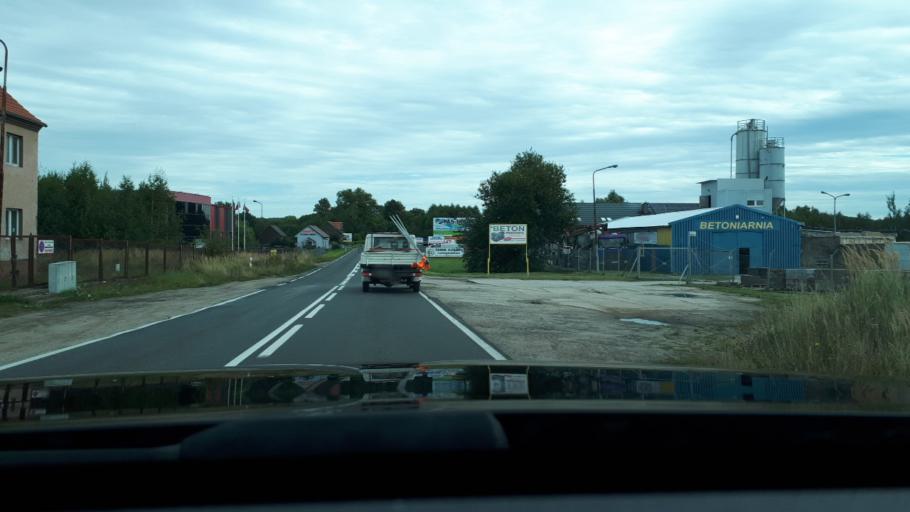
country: PL
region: Lower Silesian Voivodeship
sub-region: Powiat lwowecki
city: Gryfow Slaski
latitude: 51.0373
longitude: 15.4299
